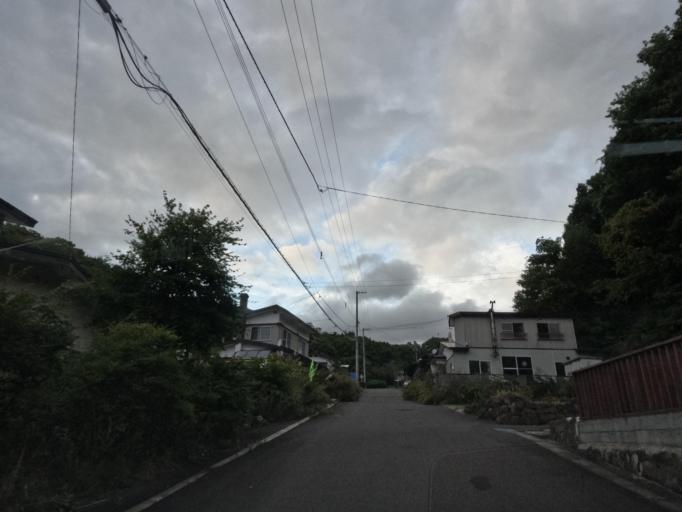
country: JP
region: Hokkaido
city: Muroran
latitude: 42.3663
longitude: 140.9653
